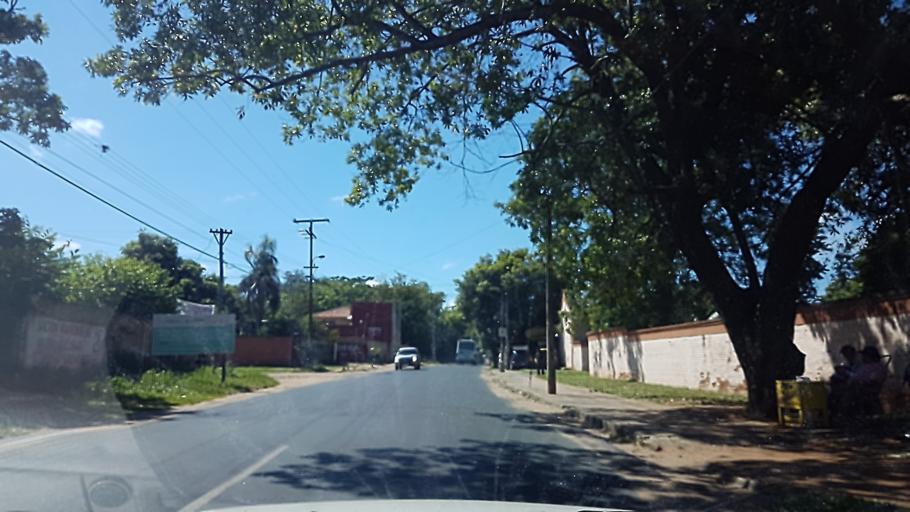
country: PY
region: Central
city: Colonia Mariano Roque Alonso
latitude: -25.2152
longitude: -57.5261
